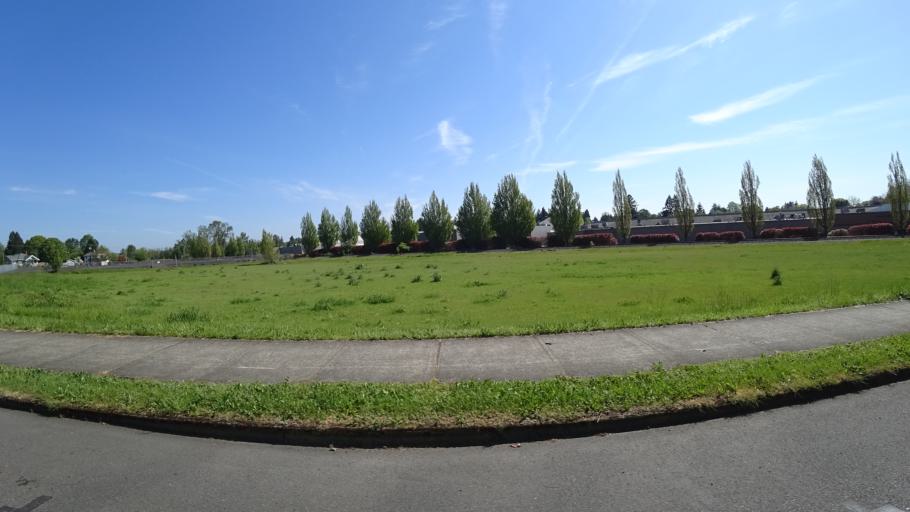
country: US
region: Oregon
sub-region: Clackamas County
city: Milwaukie
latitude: 45.4452
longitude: -122.6271
